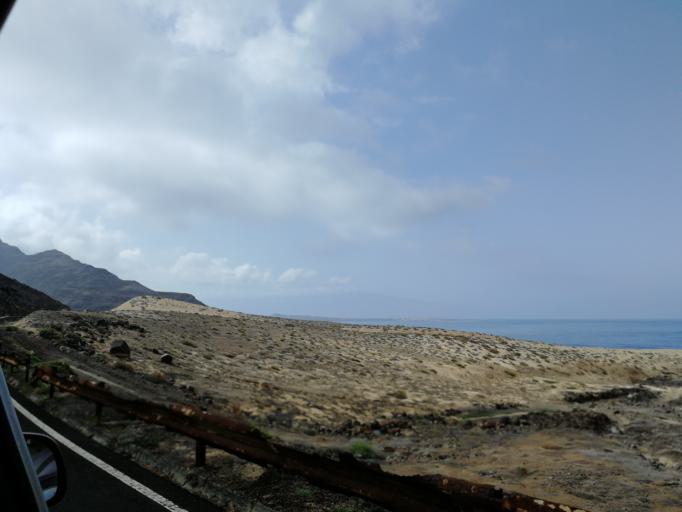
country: CV
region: Sao Vicente
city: Mindelo
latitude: 16.8600
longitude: -24.8897
